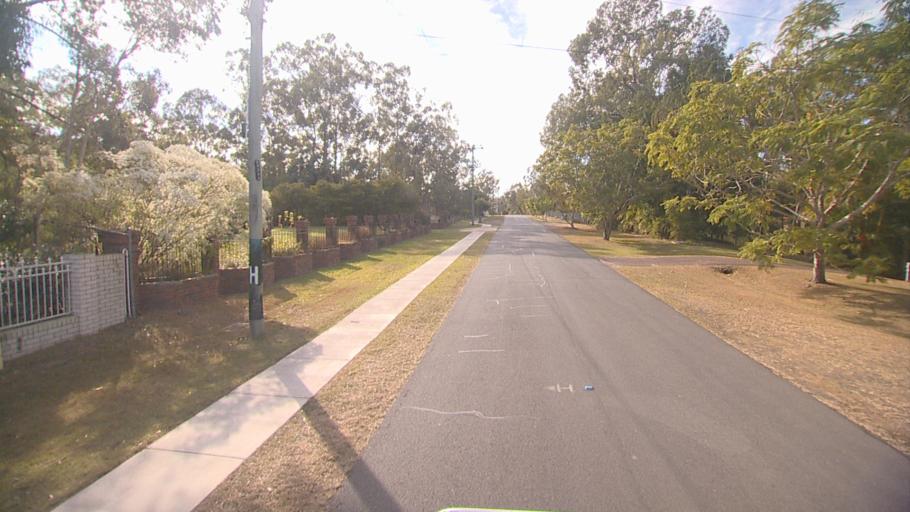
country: AU
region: Queensland
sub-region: Brisbane
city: Forest Lake
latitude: -27.6648
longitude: 153.0062
